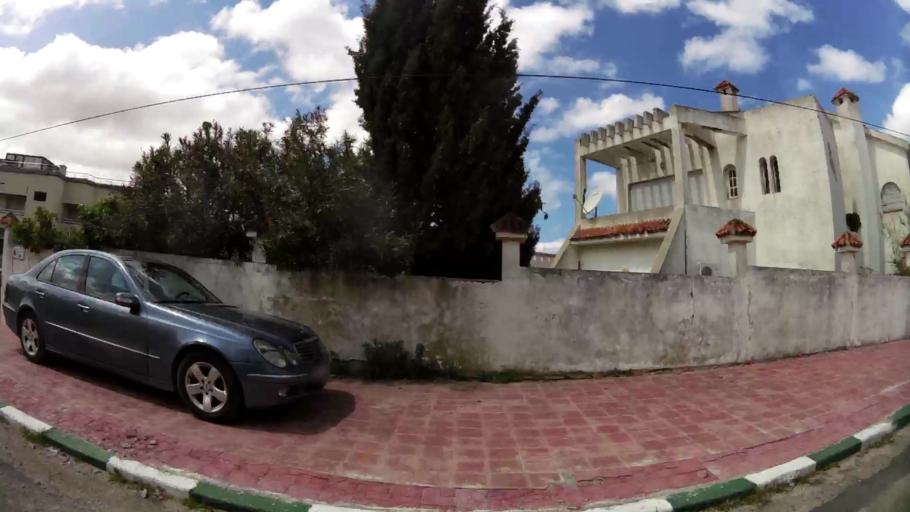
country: MA
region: Tanger-Tetouan
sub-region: Tanger-Assilah
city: Tangier
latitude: 35.7764
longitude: -5.7737
